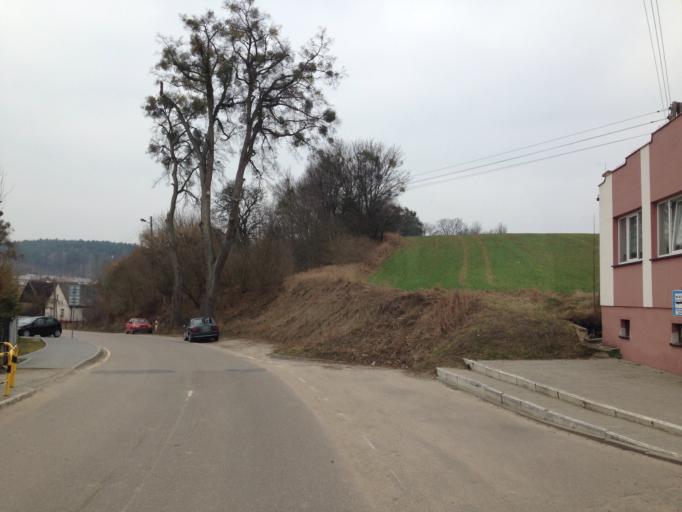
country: PL
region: Pomeranian Voivodeship
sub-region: Powiat kwidzynski
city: Sadlinki
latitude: 53.7425
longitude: 18.8201
